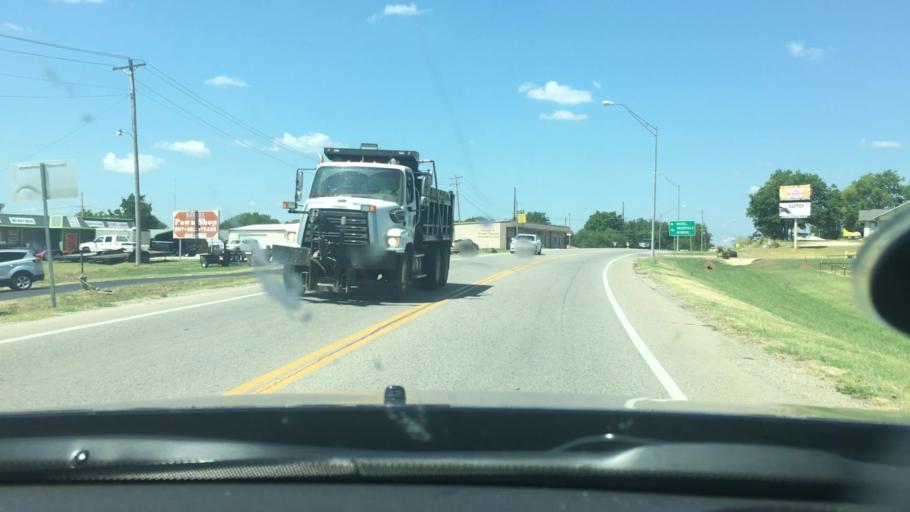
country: US
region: Oklahoma
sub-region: Marshall County
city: Kingston
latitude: 33.9977
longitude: -96.7125
